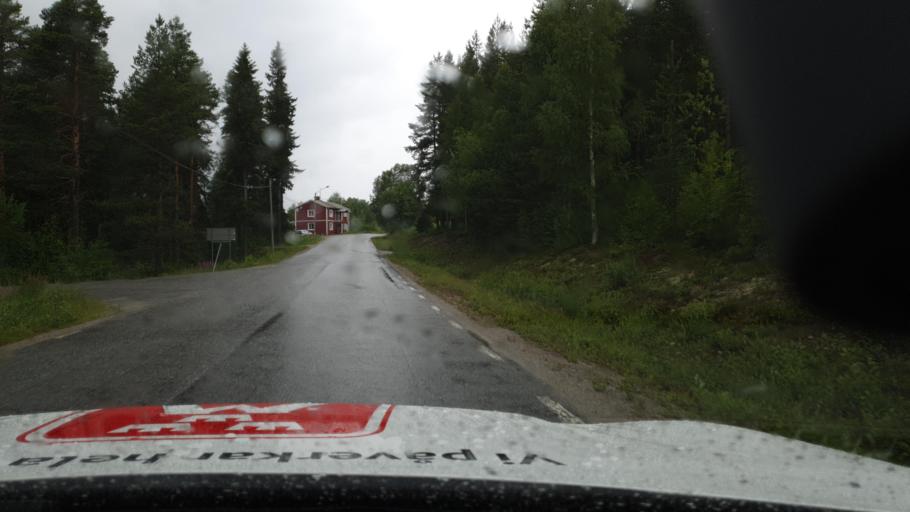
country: SE
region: Vaesterbotten
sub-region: Vindelns Kommun
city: Vindeln
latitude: 64.4055
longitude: 19.6573
